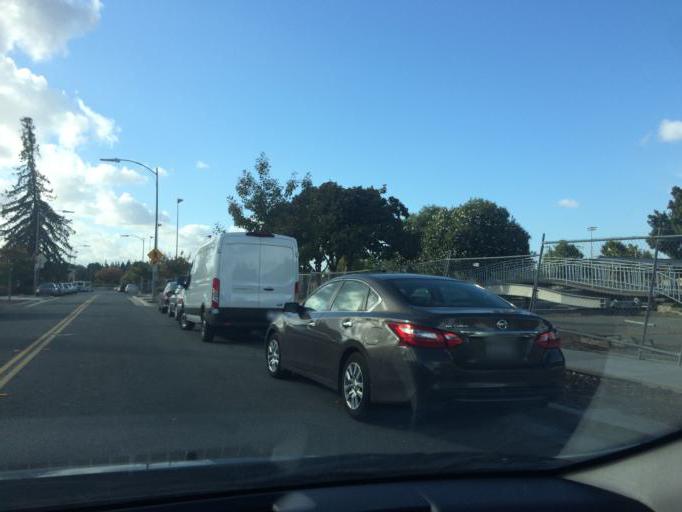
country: US
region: California
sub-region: Santa Clara County
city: Seven Trees
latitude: 37.2498
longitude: -121.7986
